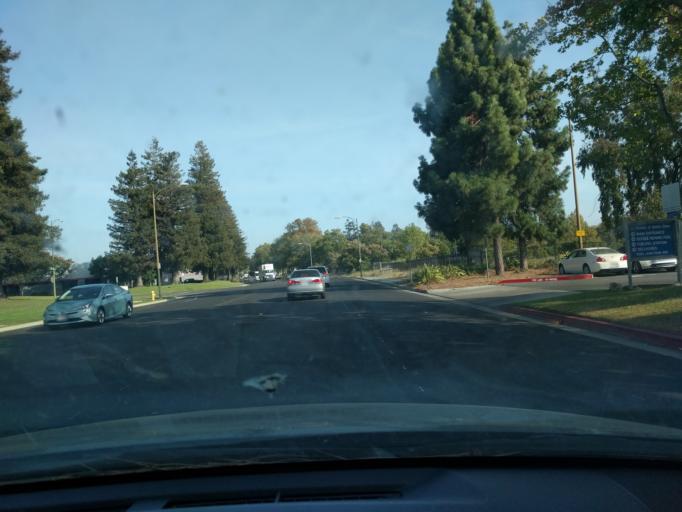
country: US
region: California
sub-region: Santa Clara County
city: Milpitas
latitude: 37.3865
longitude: -121.9164
